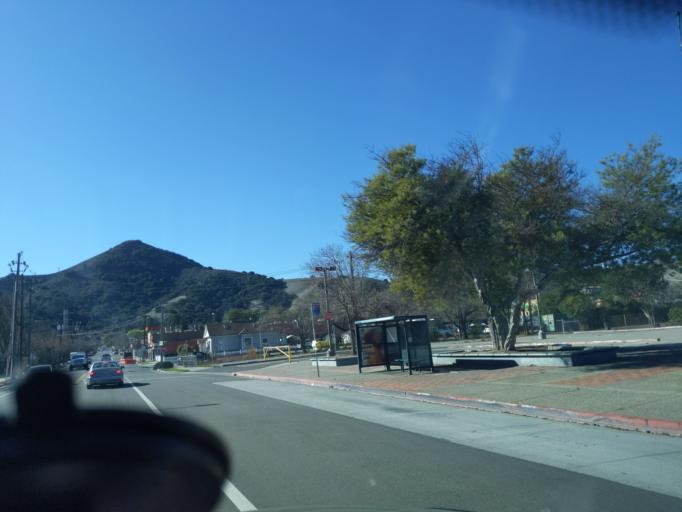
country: US
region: California
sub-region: Santa Clara County
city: Morgan Hill
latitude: 37.1287
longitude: -121.6575
